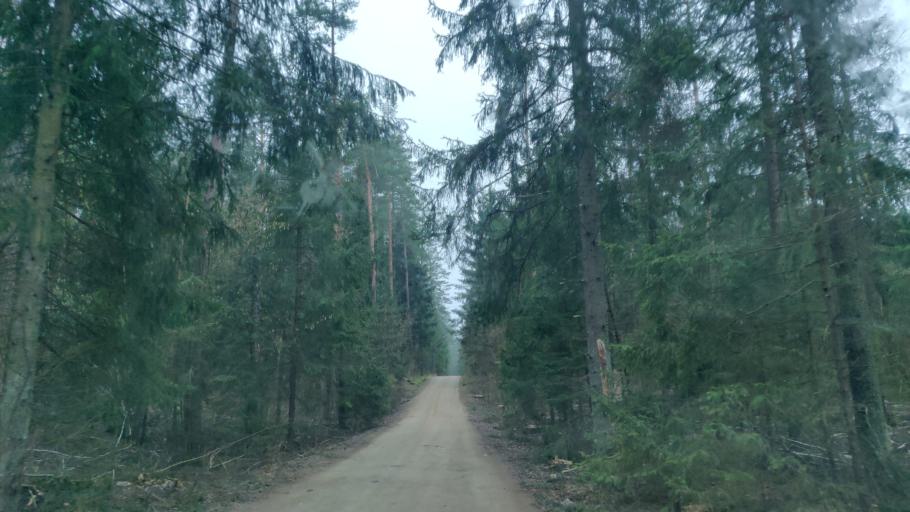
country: LT
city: Trakai
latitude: 54.5665
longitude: 24.9649
